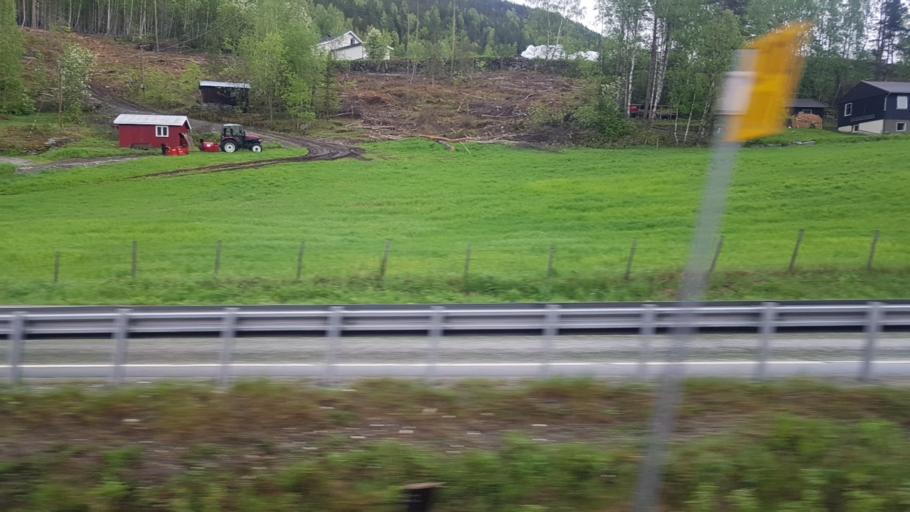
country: NO
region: Oppland
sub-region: Nord-Fron
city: Vinstra
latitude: 61.6066
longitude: 9.7251
